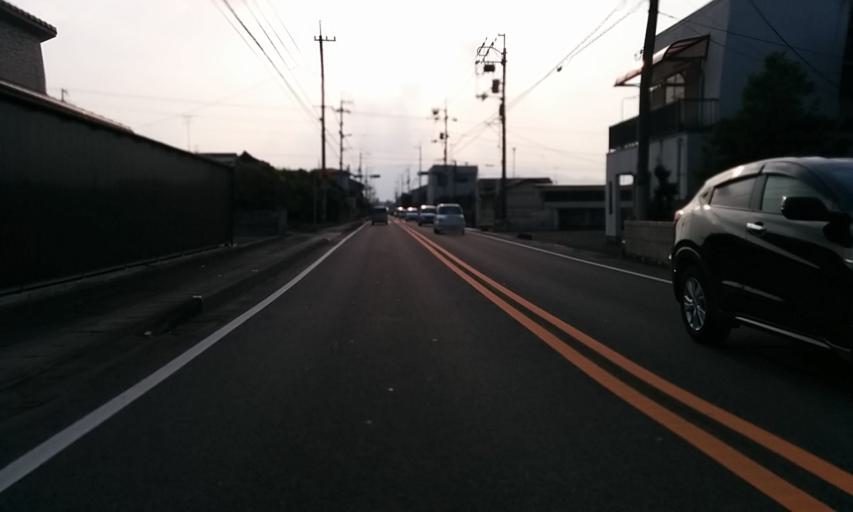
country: JP
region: Ehime
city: Saijo
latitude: 33.8949
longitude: 133.1479
